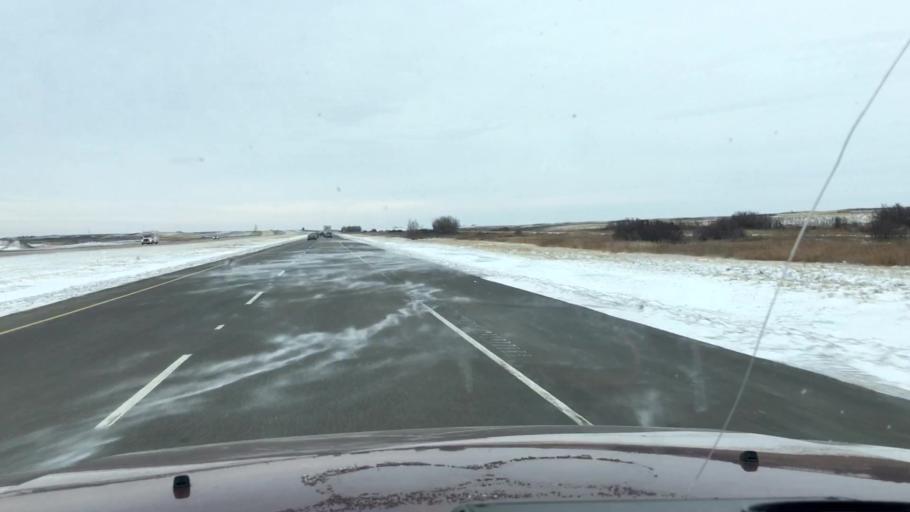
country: CA
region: Saskatchewan
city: Moose Jaw
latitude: 50.8917
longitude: -105.6267
